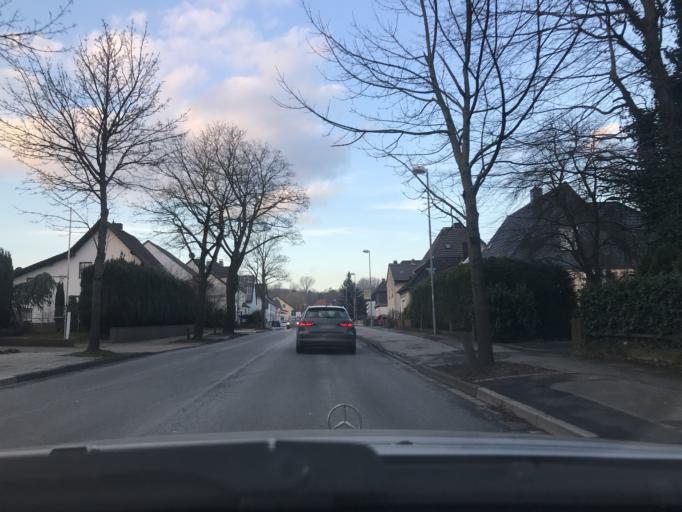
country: DE
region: North Rhine-Westphalia
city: Wickede
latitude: 51.4990
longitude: 7.8703
